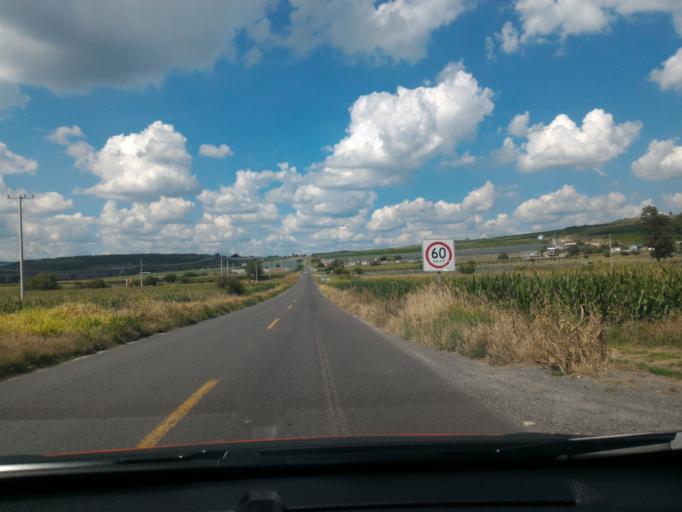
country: MX
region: Guanajuato
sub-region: Penjamo
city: Estacion la Piedad
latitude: 20.4131
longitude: -101.9963
